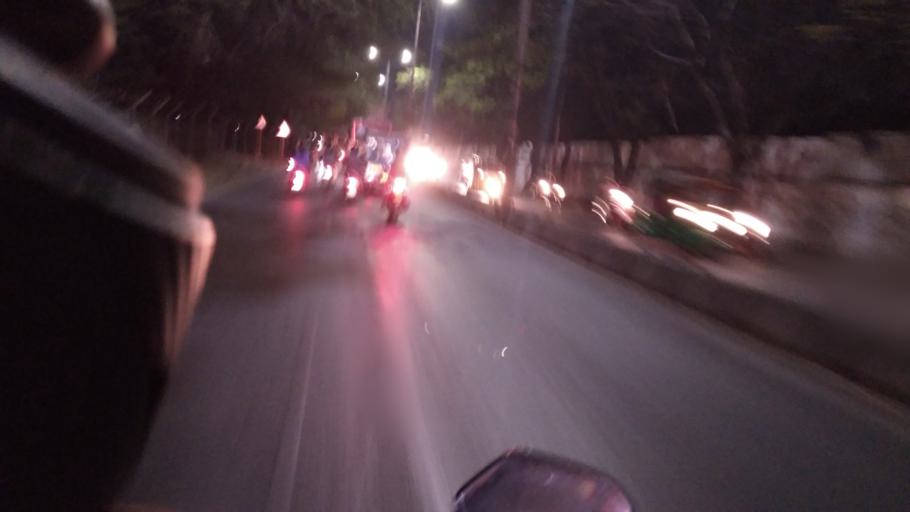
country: IN
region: Telangana
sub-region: Hyderabad
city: Malkajgiri
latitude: 17.4555
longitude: 78.4800
